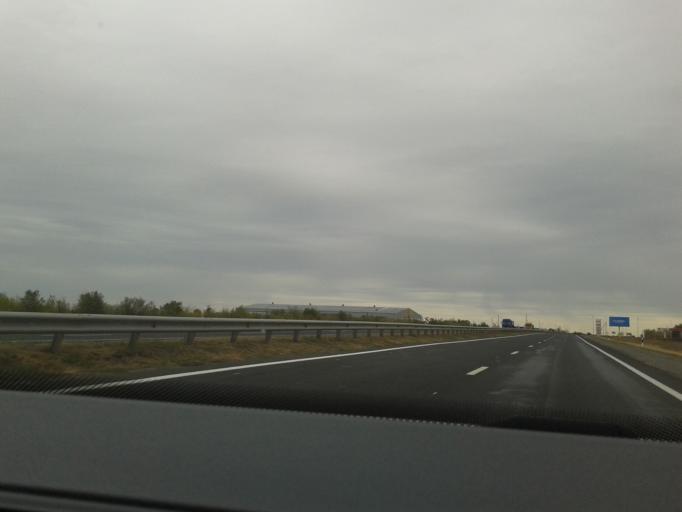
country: RU
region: Volgograd
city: Gorodishche
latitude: 48.8310
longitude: 44.4219
